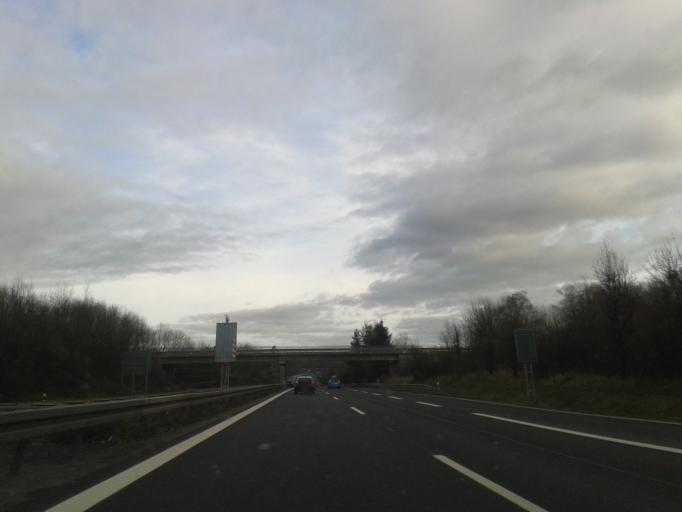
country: DE
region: Saxony
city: Ohorn
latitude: 51.1639
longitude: 14.0494
